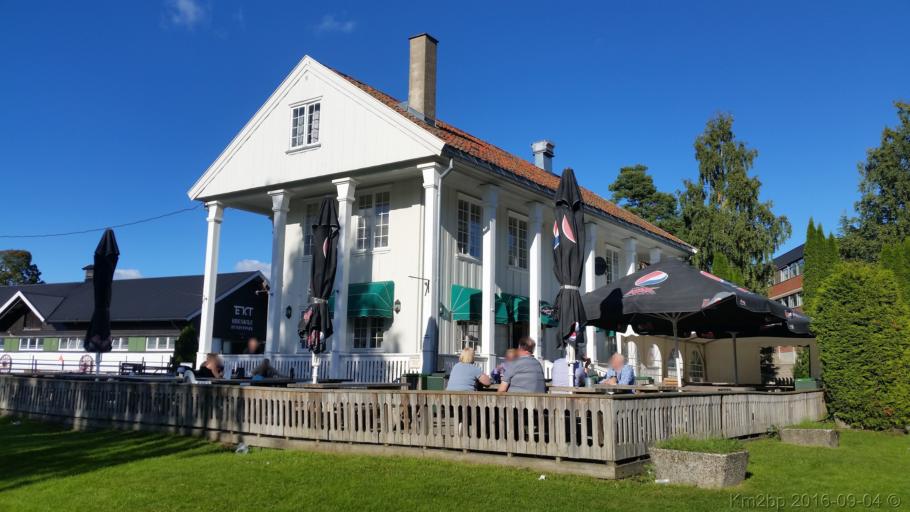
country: NO
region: Oslo
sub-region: Oslo
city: Oslo
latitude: 59.8914
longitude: 10.7748
